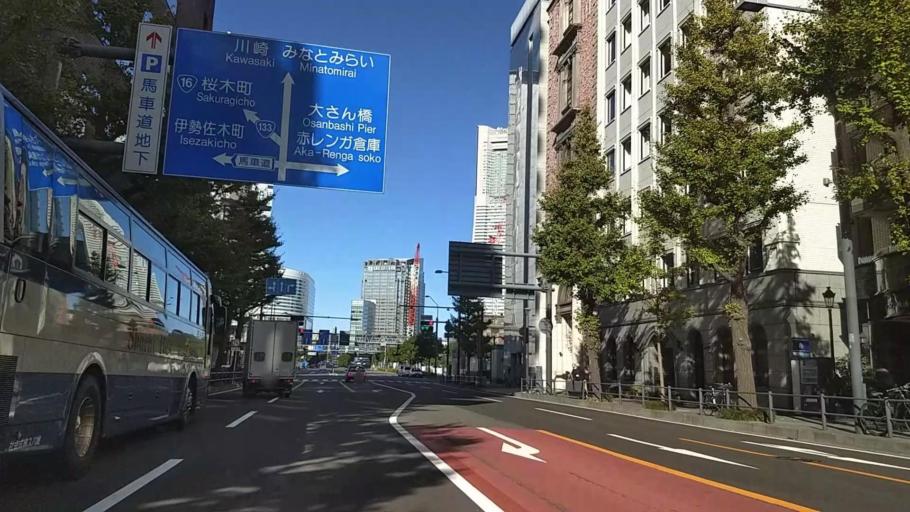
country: JP
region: Kanagawa
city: Yokohama
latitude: 35.4493
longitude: 139.6378
